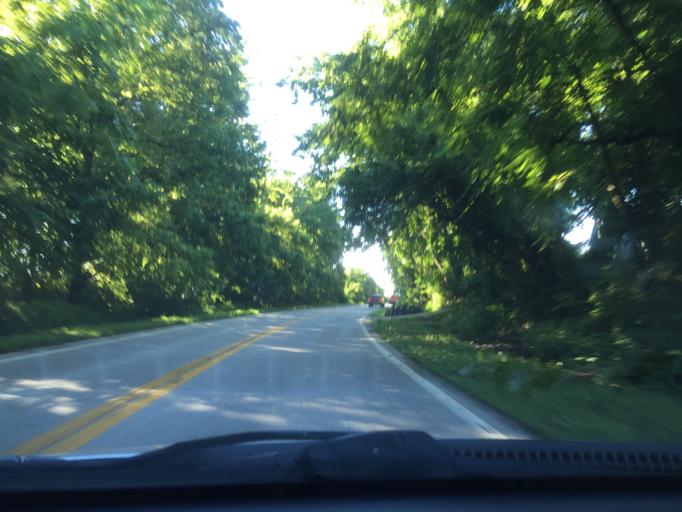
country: US
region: Maryland
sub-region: Baltimore County
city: Hunt Valley
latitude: 39.5472
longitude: -76.6628
